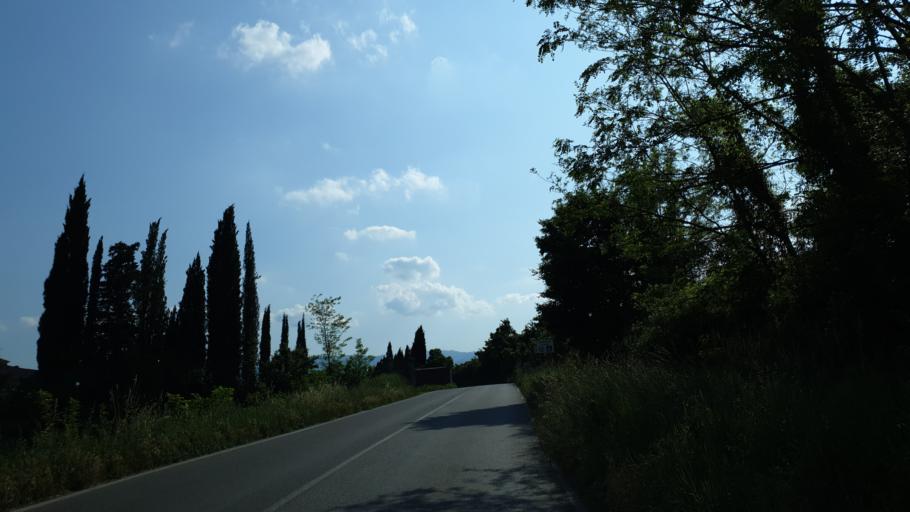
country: IT
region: Tuscany
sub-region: Province of Arezzo
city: Soci
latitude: 43.7440
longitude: 11.8164
